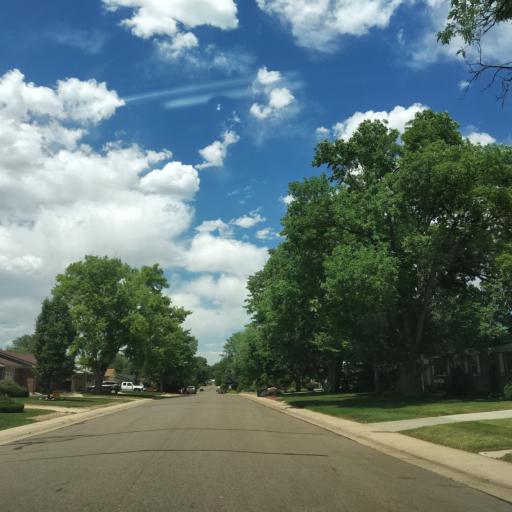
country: US
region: Colorado
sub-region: Jefferson County
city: Lakewood
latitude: 39.6865
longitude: -105.0927
